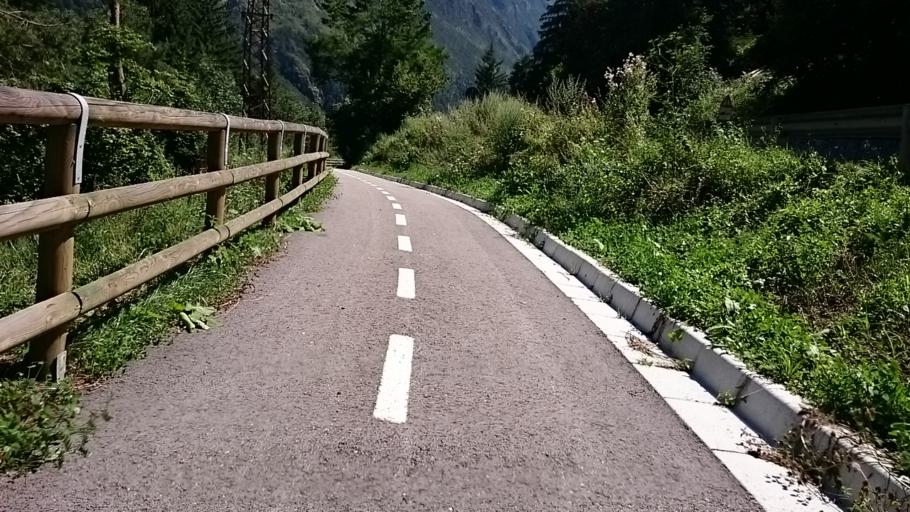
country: IT
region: Veneto
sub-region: Provincia di Belluno
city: Pieve di Cadore
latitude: 46.4085
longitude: 12.3673
